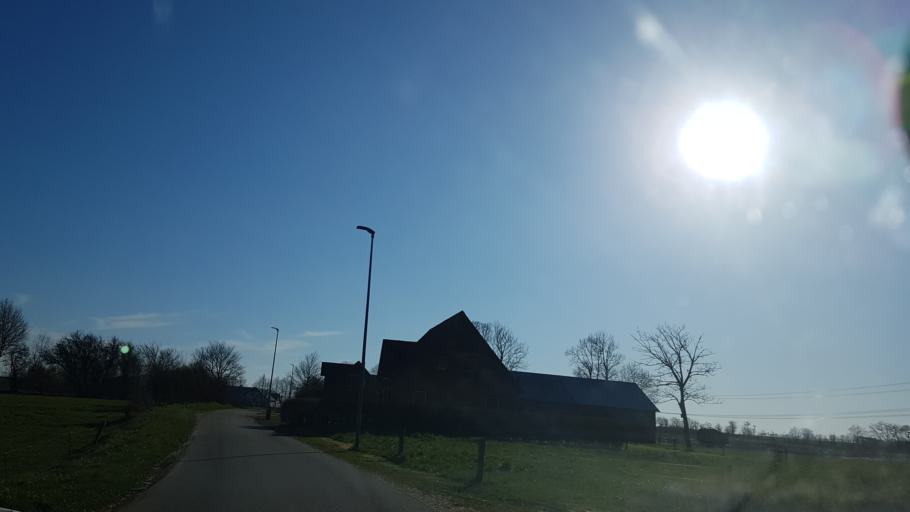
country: DK
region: South Denmark
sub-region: Vejen Kommune
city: Vejen
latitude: 55.4377
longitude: 9.1821
